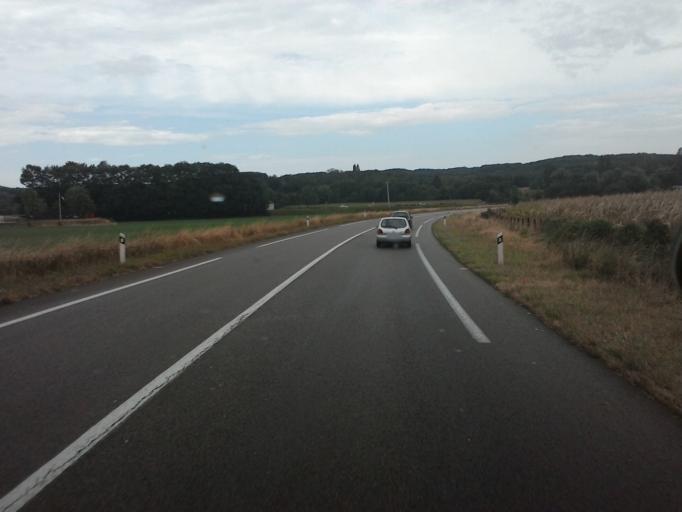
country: FR
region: Franche-Comte
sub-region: Departement du Jura
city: Poligny
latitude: 46.8374
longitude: 5.6960
